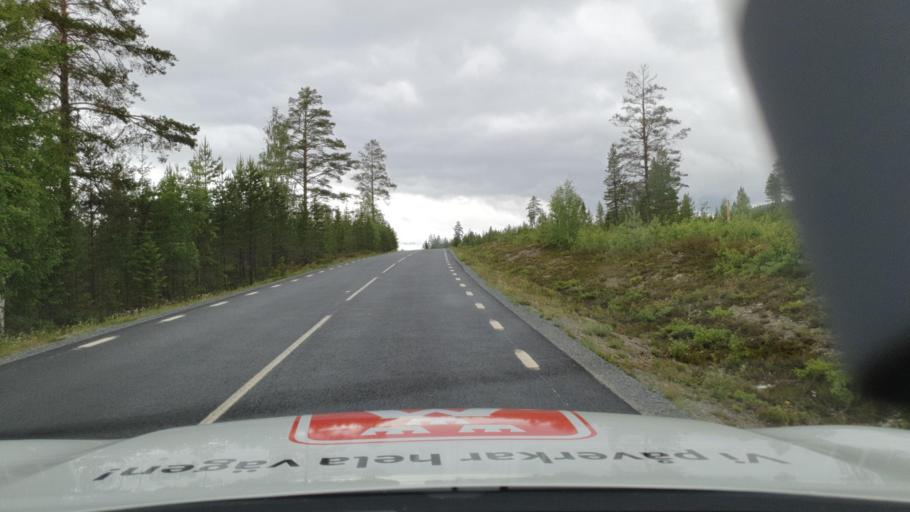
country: SE
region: Vaesterbotten
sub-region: Dorotea Kommun
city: Dorotea
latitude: 64.2046
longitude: 16.5636
